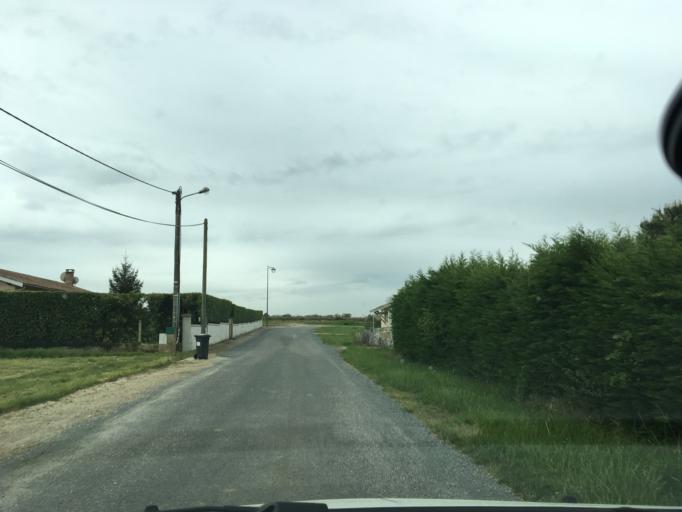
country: FR
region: Aquitaine
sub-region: Departement de la Gironde
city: Lesparre-Medoc
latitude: 45.3109
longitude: -0.8934
